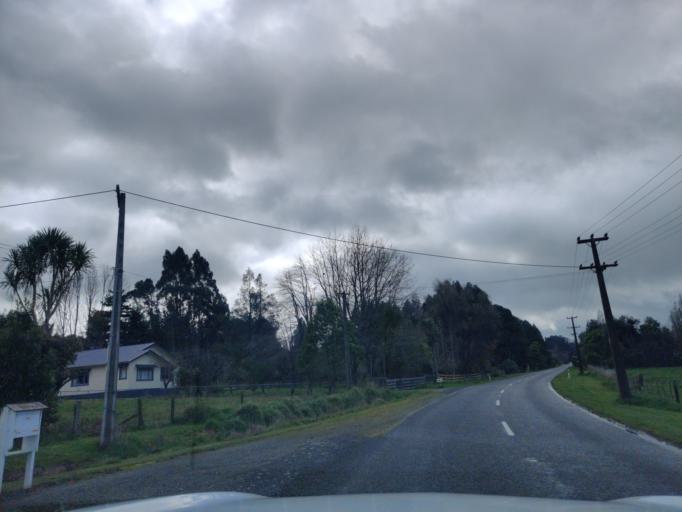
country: NZ
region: Manawatu-Wanganui
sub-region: Palmerston North City
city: Palmerston North
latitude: -40.1773
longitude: 175.7900
